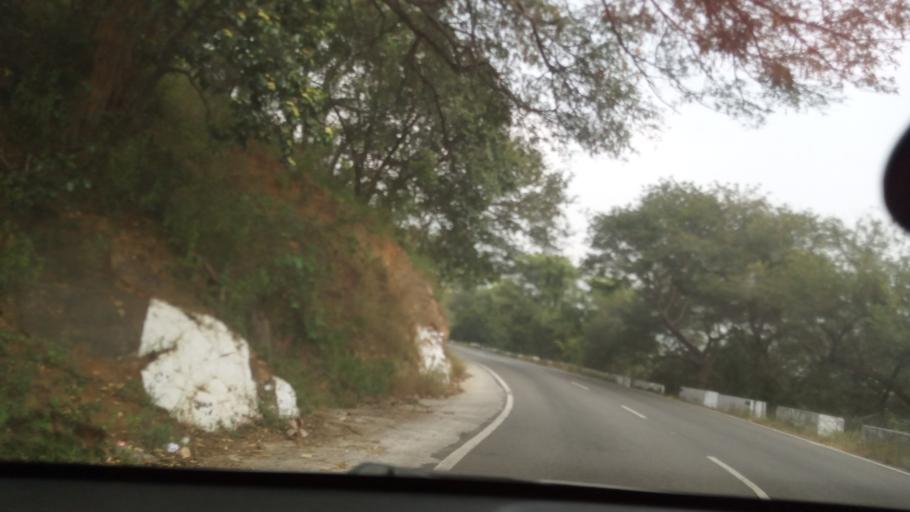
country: IN
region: Tamil Nadu
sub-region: Erode
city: Sathyamangalam
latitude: 11.5862
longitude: 77.1319
